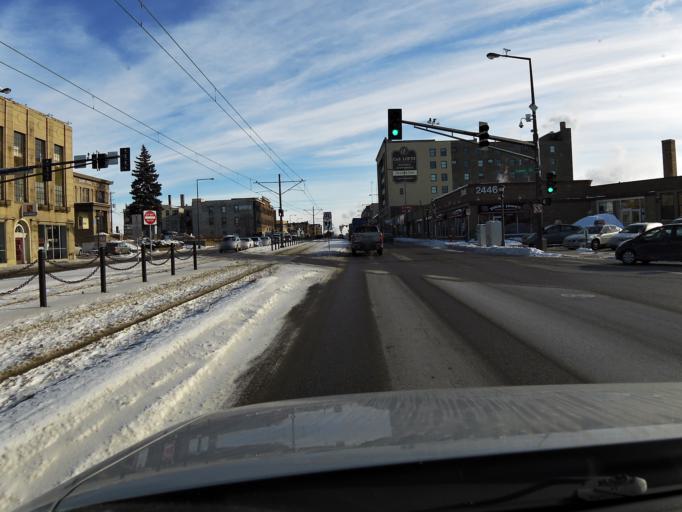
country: US
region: Minnesota
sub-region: Ramsey County
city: Lauderdale
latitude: 44.9647
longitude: -93.1998
